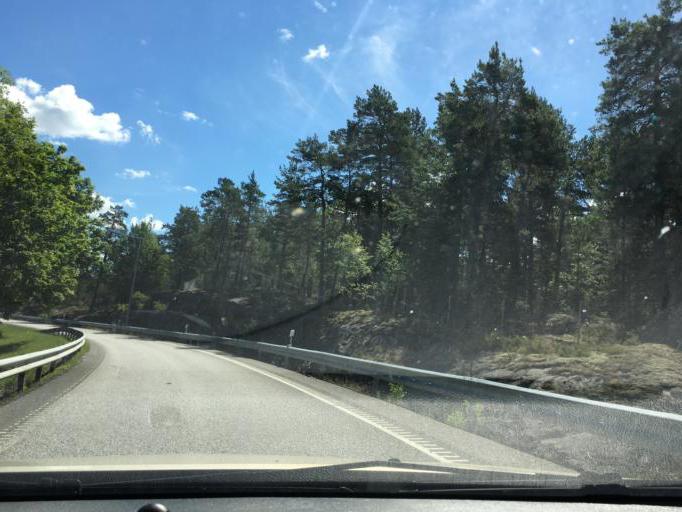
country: SE
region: Stockholm
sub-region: Nacka Kommun
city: Fisksatra
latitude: 59.2902
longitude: 18.2433
